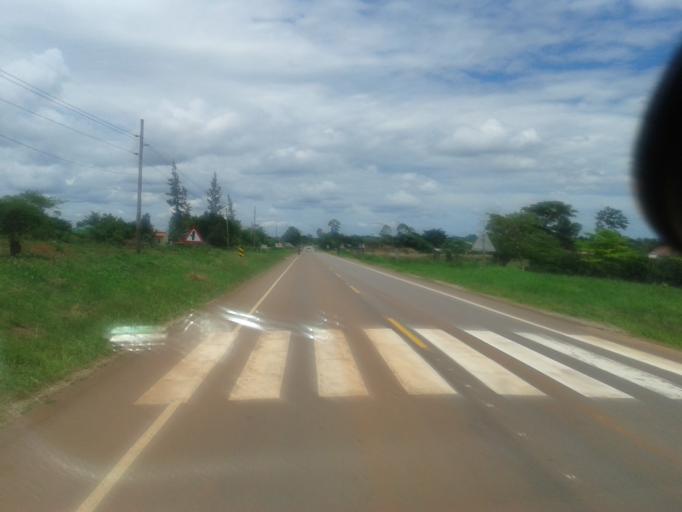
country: UG
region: Western Region
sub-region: Kiryandongo District
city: Kiryandongo
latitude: 1.7907
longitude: 32.0142
